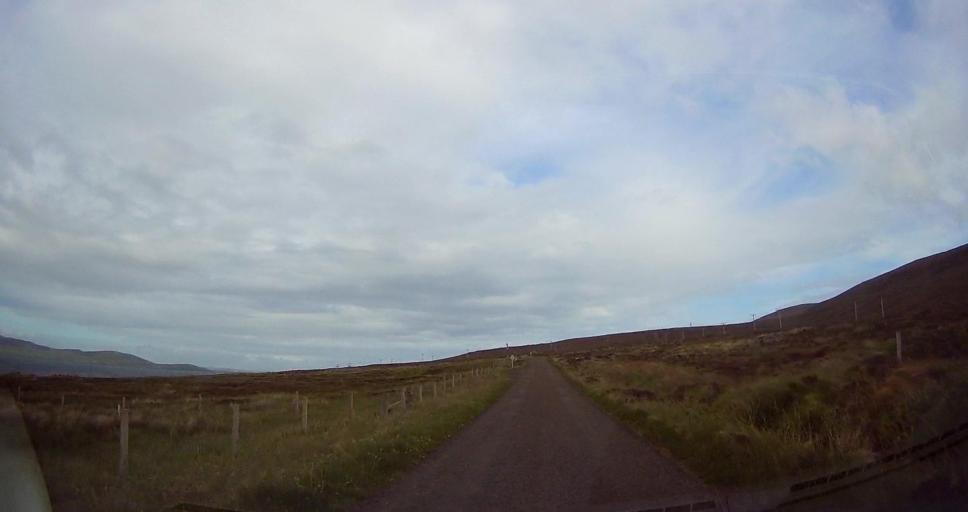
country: GB
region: Scotland
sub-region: Orkney Islands
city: Stromness
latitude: 58.9024
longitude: -3.2965
